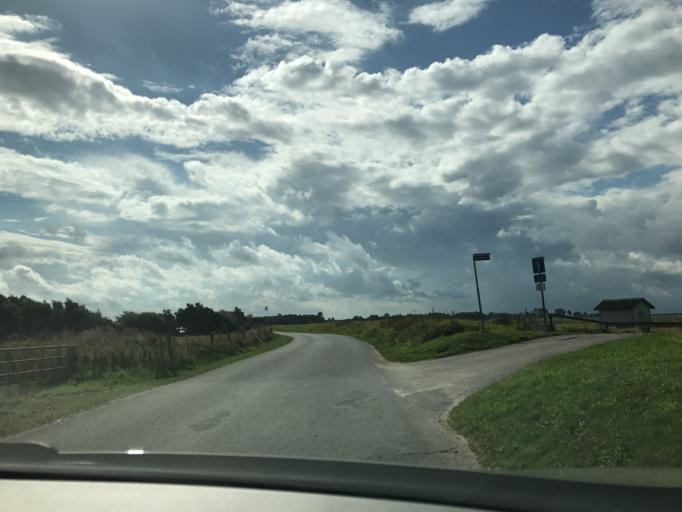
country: DK
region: South Denmark
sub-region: Middelfart Kommune
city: Norre Aby
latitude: 55.4234
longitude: 9.8292
